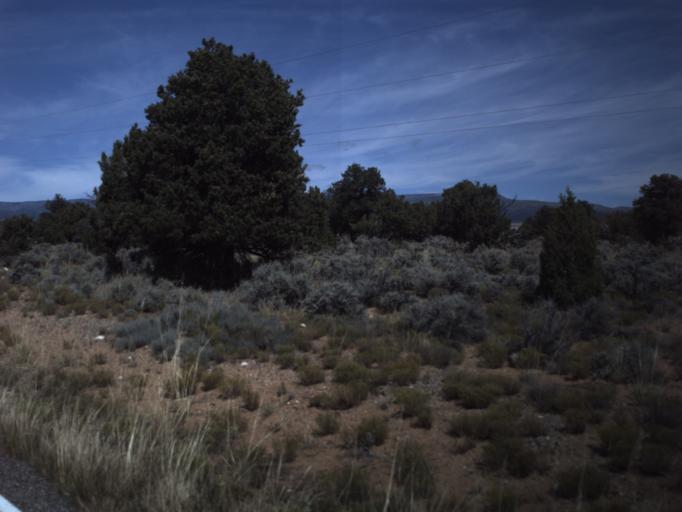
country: US
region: Utah
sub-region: Wayne County
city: Loa
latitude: 37.8505
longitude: -111.4297
